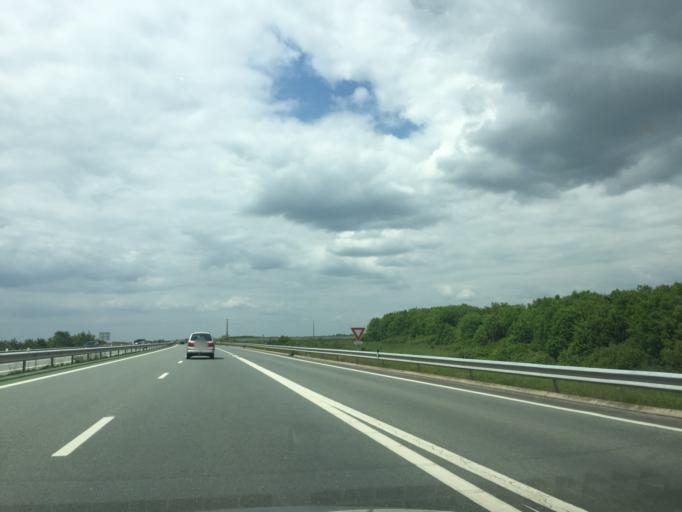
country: FR
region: Poitou-Charentes
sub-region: Departement des Deux-Sevres
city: Echire
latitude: 46.4160
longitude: -0.4004
